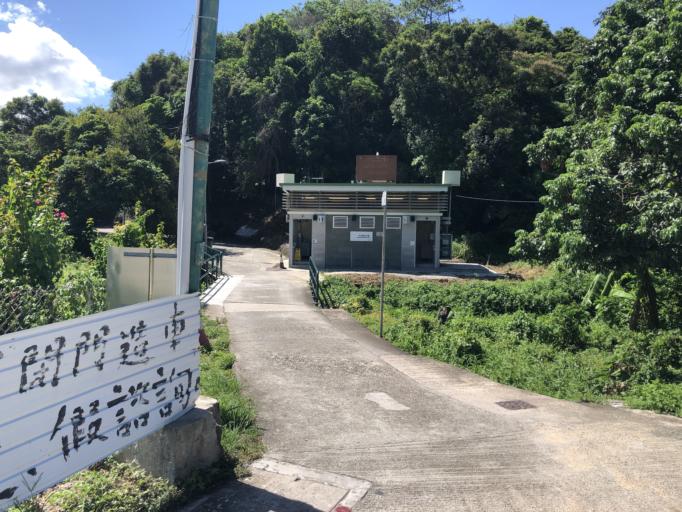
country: HK
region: Tuen Mun
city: Tuen Mun
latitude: 22.2917
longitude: 113.9778
